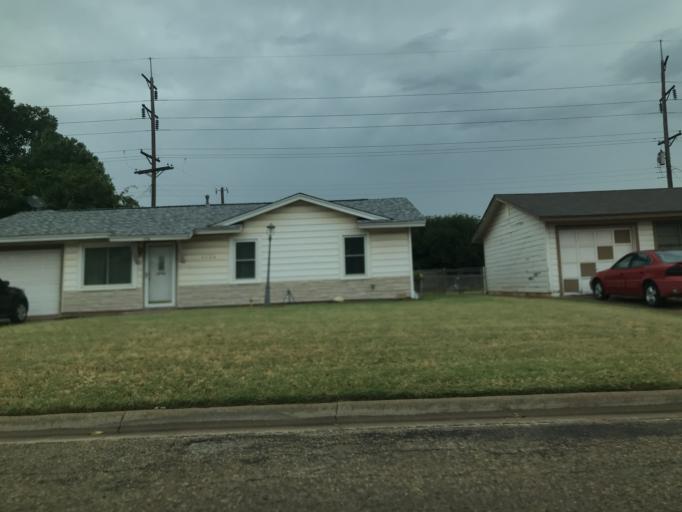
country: US
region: Texas
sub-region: Taylor County
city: Abilene
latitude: 32.4173
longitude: -99.7850
